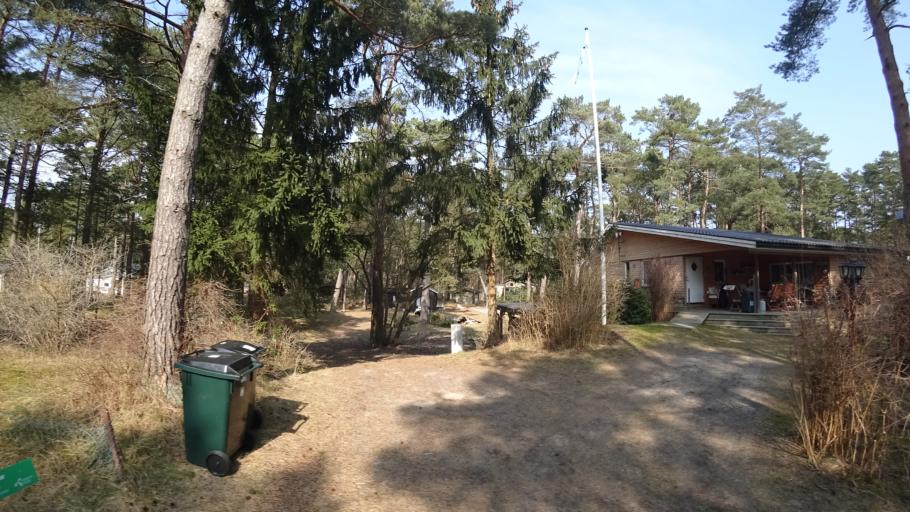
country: SE
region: Skane
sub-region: Kristianstads Kommun
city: Ahus
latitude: 55.9430
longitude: 14.3182
